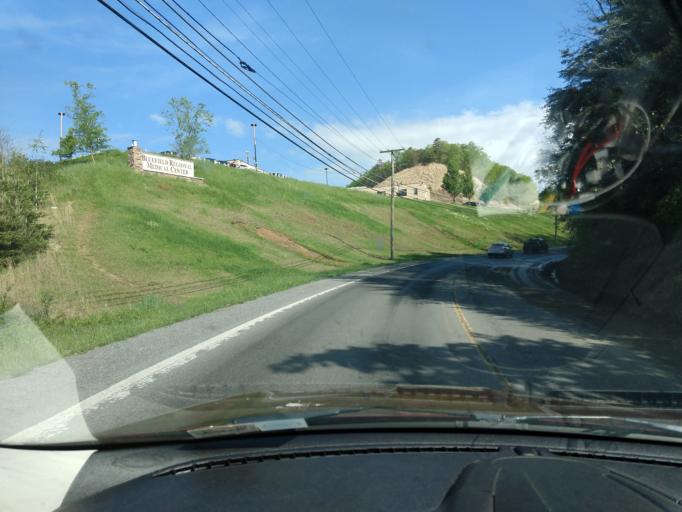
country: US
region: West Virginia
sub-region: Mercer County
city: Bluefield
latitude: 37.2549
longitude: -81.2339
